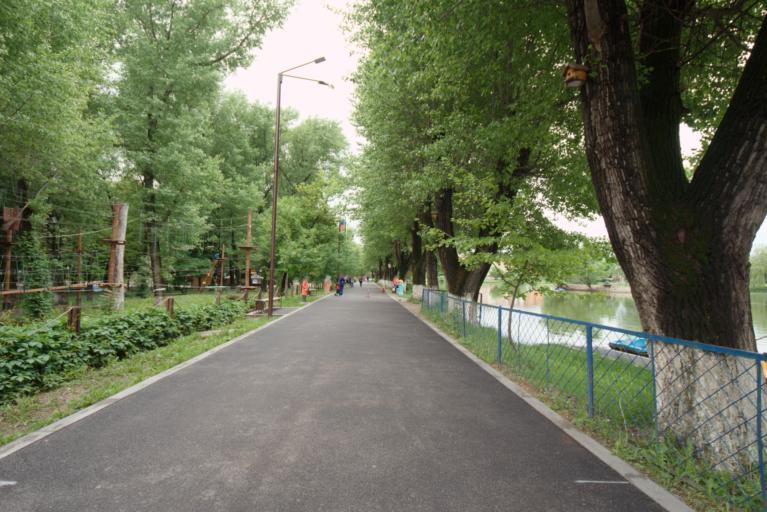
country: RU
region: Stavropol'skiy
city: Svobody
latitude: 44.0331
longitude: 43.0605
